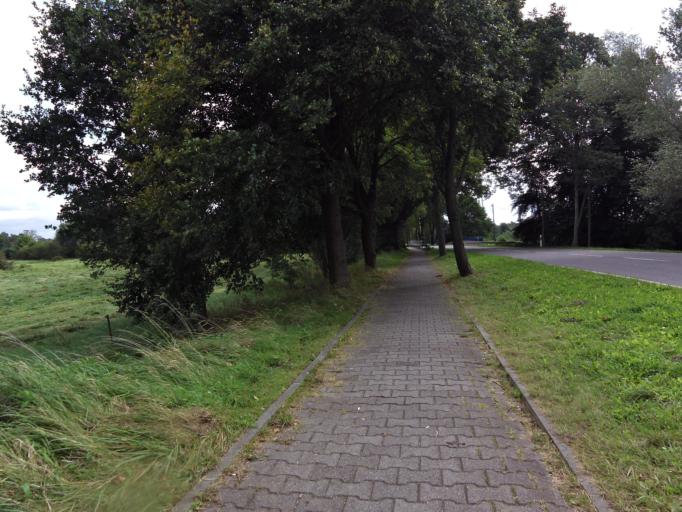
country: DE
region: Saxony-Anhalt
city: Havelberg
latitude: 52.8241
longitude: 12.0625
